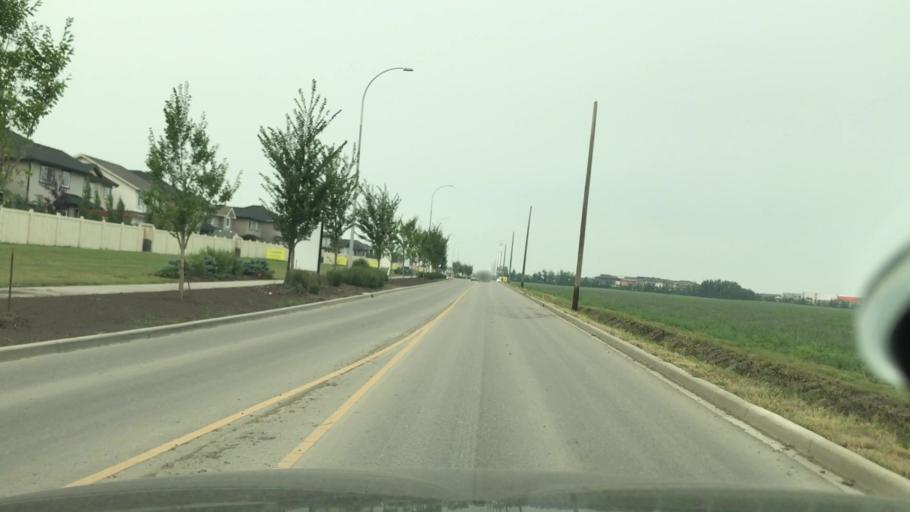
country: CA
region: Alberta
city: Devon
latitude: 53.4249
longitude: -113.5925
